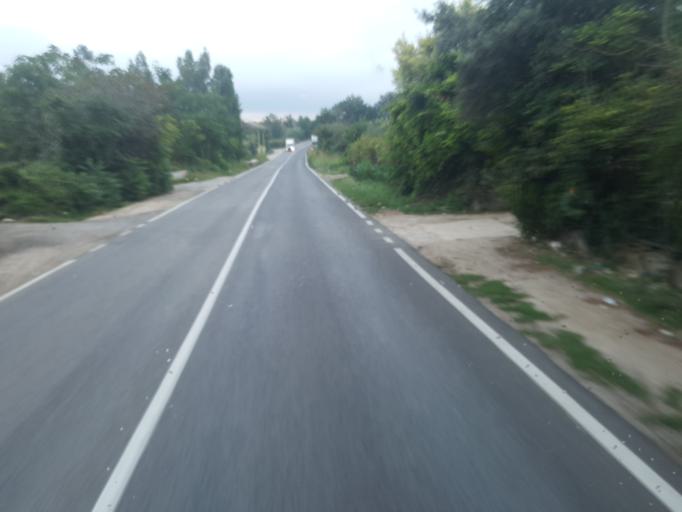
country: IT
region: Campania
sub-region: Provincia di Caserta
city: Sparanise
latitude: 41.1754
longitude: 14.1231
